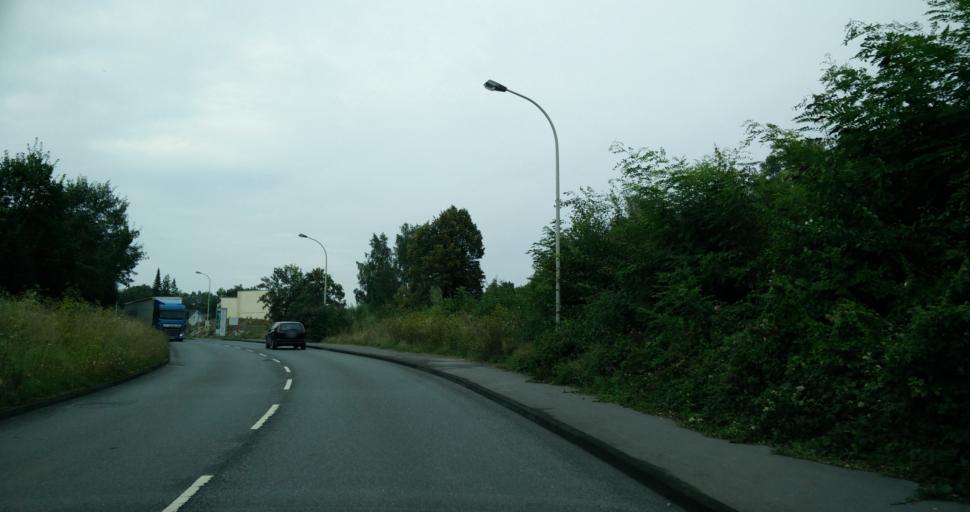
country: DE
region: North Rhine-Westphalia
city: Wulfrath
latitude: 51.2525
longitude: 7.0605
